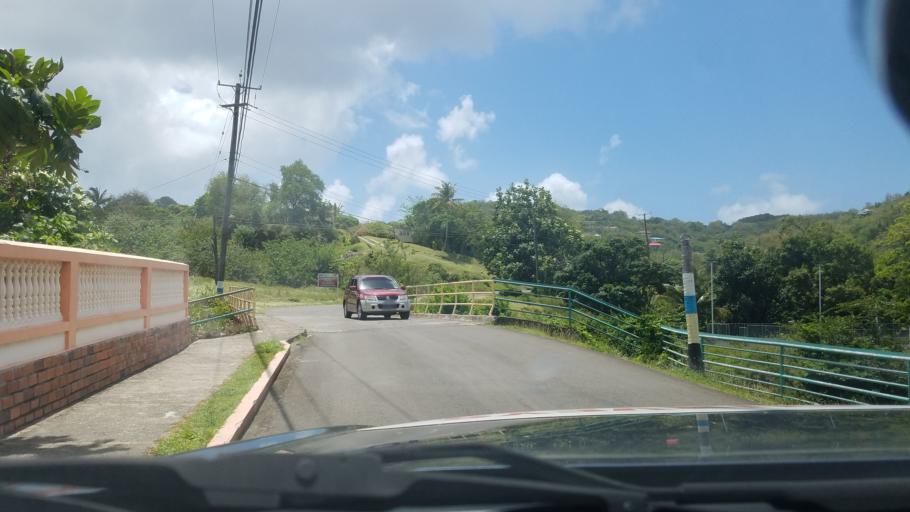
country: LC
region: Gros-Islet
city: Gros Islet
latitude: 14.0535
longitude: -60.9309
